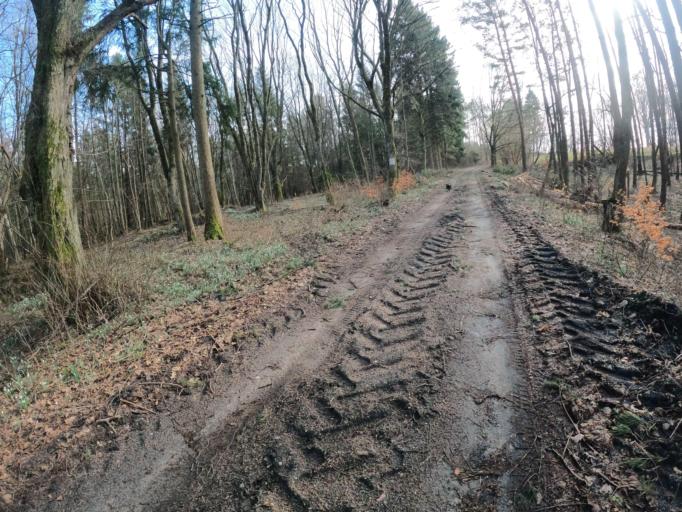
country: PL
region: West Pomeranian Voivodeship
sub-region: Powiat koszalinski
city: Bobolice
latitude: 53.9813
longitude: 16.5691
